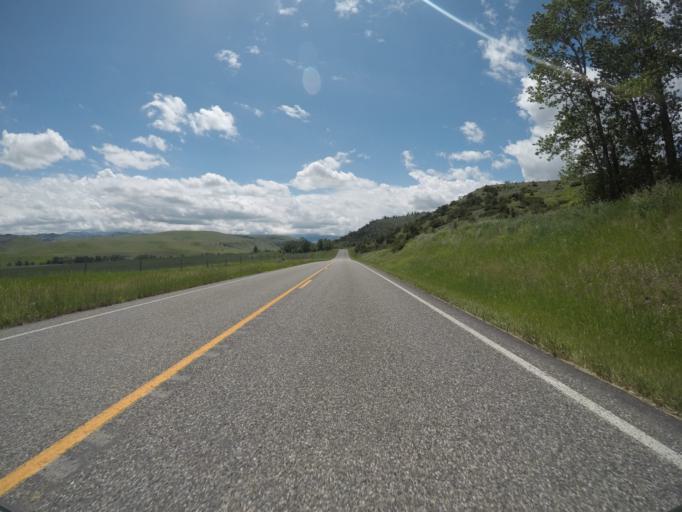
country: US
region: Montana
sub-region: Sweet Grass County
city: Big Timber
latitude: 45.6811
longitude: -110.0859
